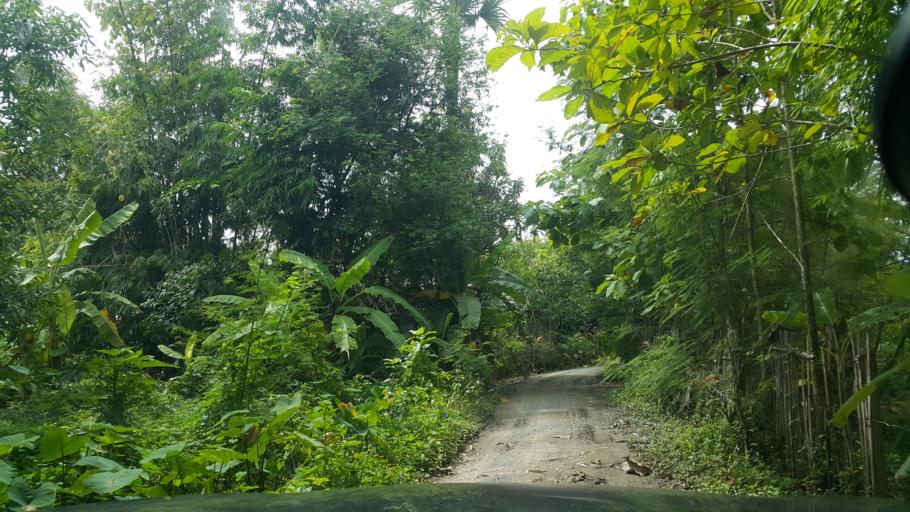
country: TH
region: Chiang Mai
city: San Kamphaeng
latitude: 18.7601
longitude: 99.1655
